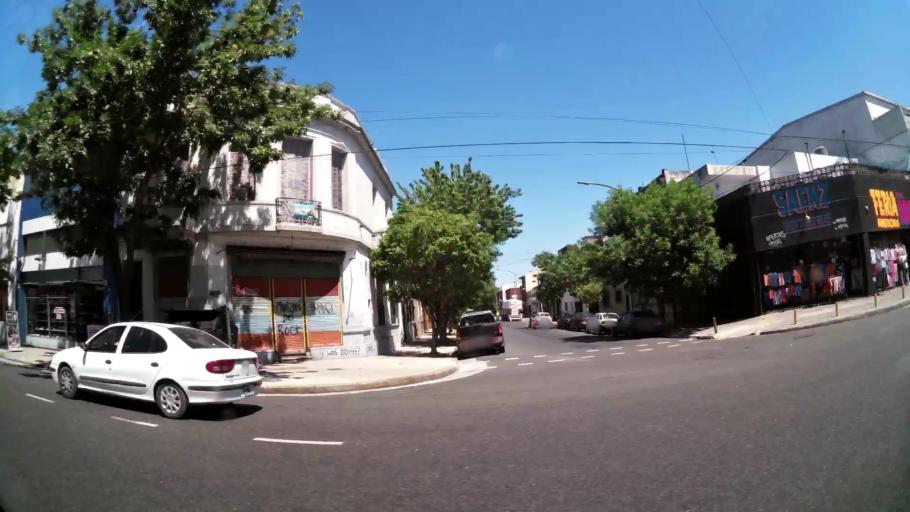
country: AR
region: Buenos Aires
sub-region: Partido de Avellaneda
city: Avellaneda
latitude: -34.6463
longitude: -58.4162
